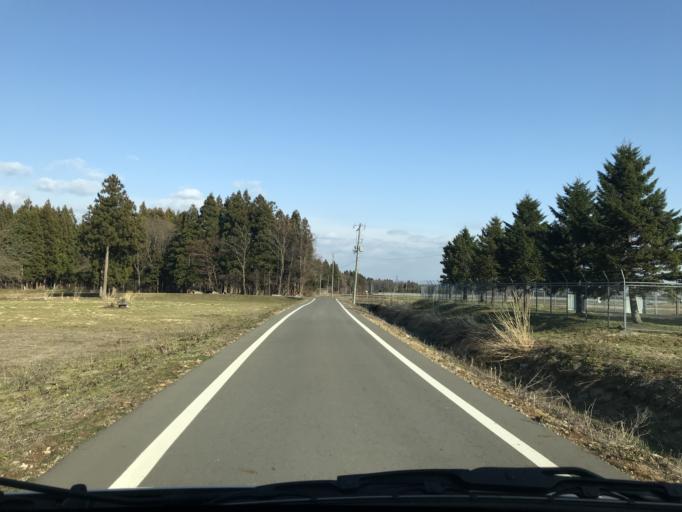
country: JP
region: Iwate
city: Kitakami
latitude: 39.2748
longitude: 141.0686
